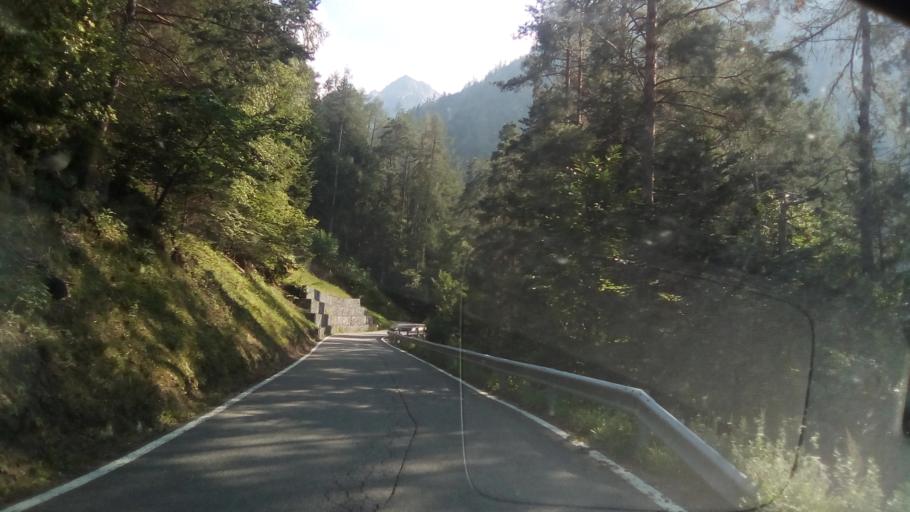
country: CH
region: Valais
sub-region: Martigny District
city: Martigny-Combe
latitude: 46.0682
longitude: 7.0733
